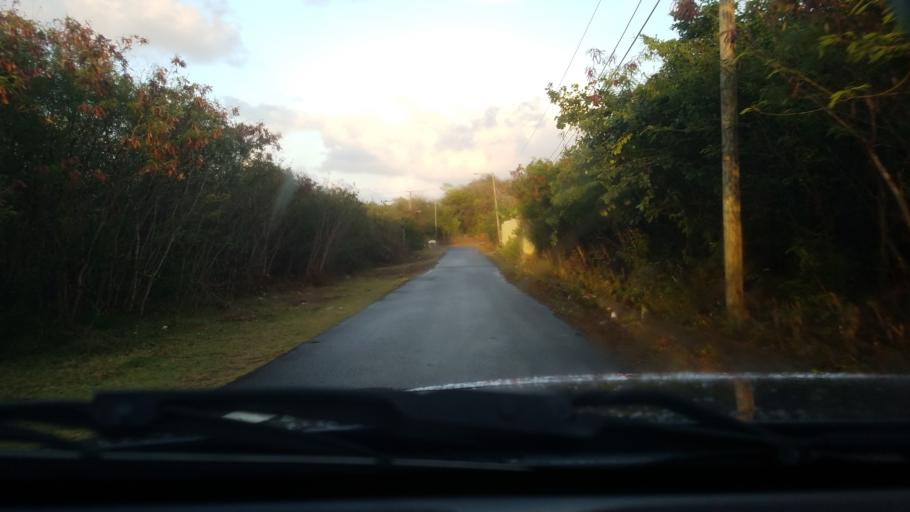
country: LC
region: Gros-Islet
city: Gros Islet
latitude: 14.0895
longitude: -60.9331
